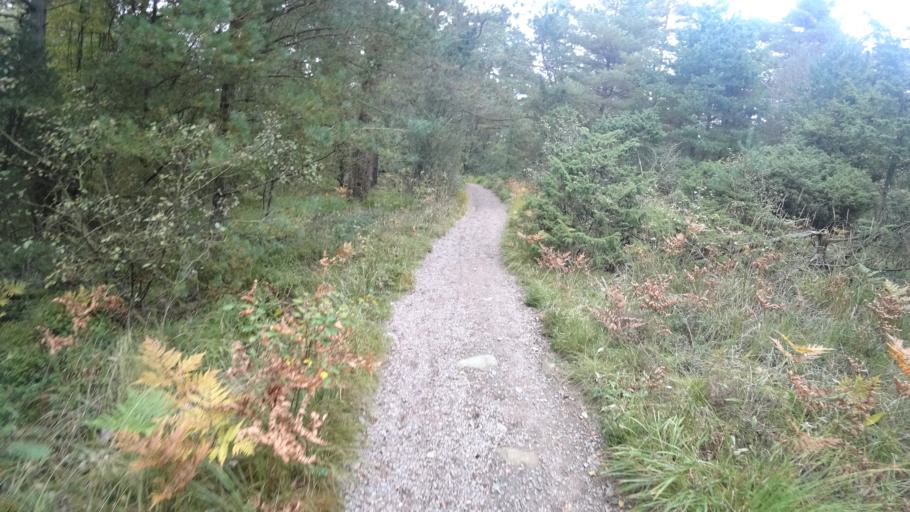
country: SE
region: Vaestra Goetaland
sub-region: Molndal
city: Moelndal
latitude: 57.6182
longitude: 11.9733
